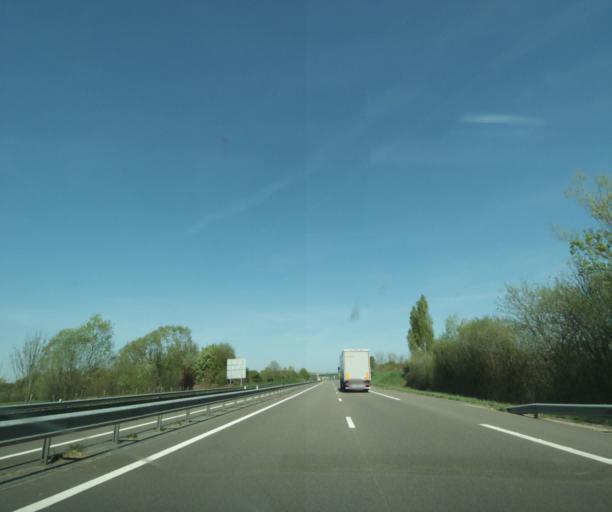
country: FR
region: Bourgogne
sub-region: Departement de la Nievre
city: Saint-Eloi
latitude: 46.9894
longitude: 3.2063
